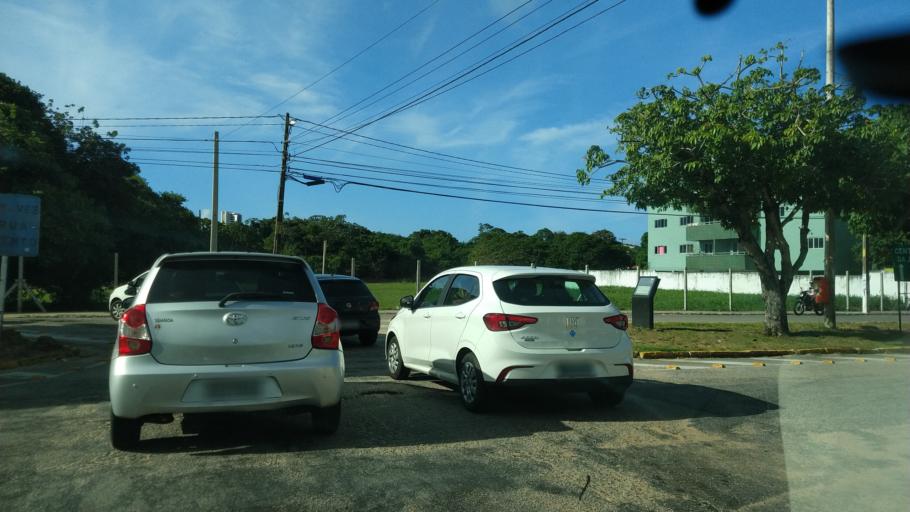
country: BR
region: Rio Grande do Norte
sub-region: Natal
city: Natal
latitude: -5.8087
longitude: -35.2004
